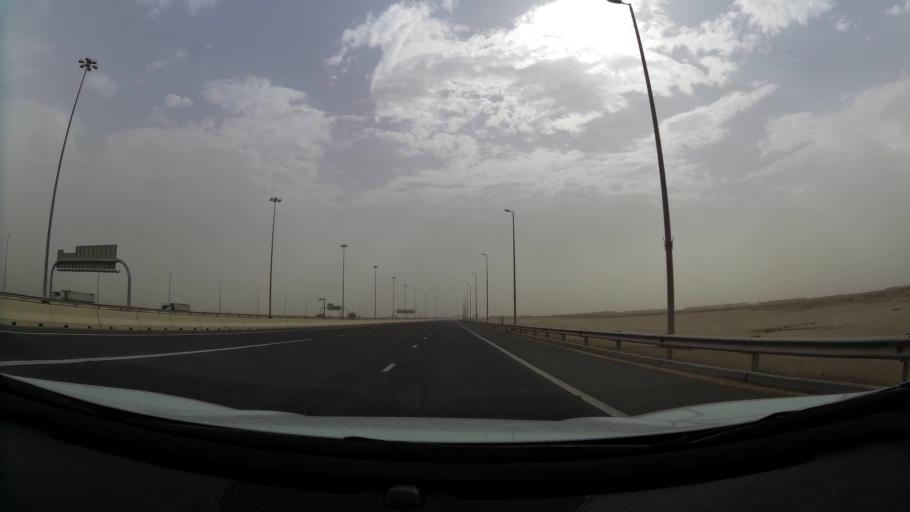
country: AE
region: Abu Dhabi
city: Abu Dhabi
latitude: 24.4823
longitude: 54.6528
